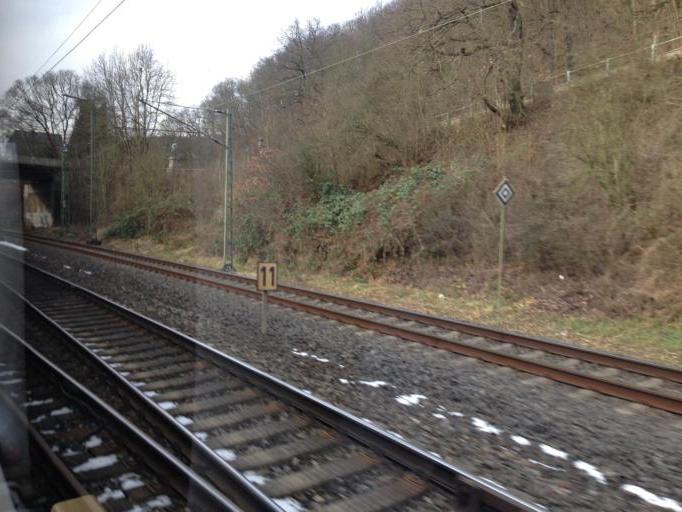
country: DE
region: Hesse
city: Dillenburg
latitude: 50.7414
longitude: 8.2895
